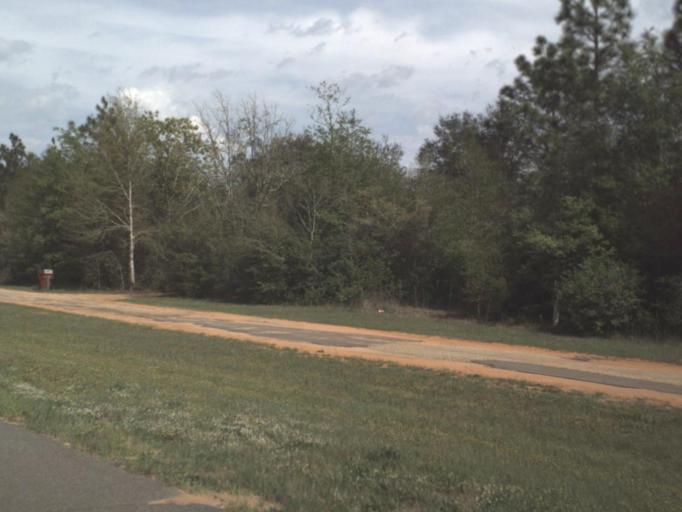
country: US
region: Florida
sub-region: Santa Rosa County
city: East Milton
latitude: 30.6817
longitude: -86.8371
